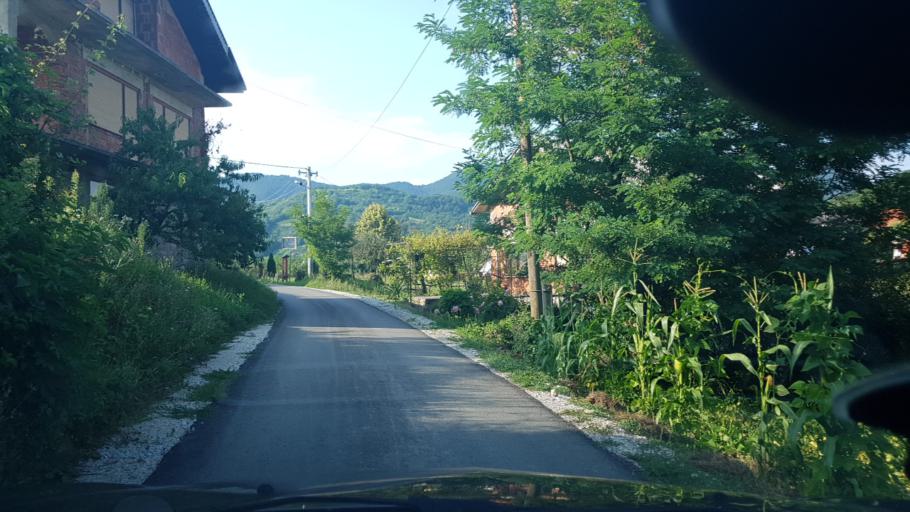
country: HR
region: Krapinsko-Zagorska
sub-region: Grad Krapina
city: Krapina
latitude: 46.1566
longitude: 15.8876
